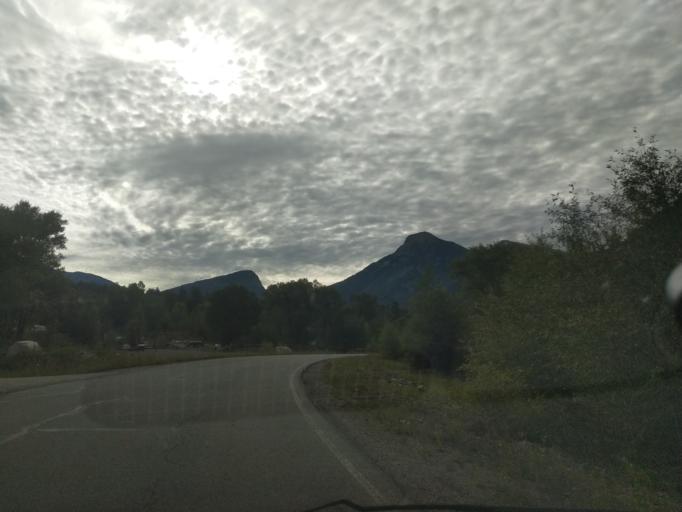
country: US
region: Colorado
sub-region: Gunnison County
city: Crested Butte
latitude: 39.0738
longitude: -107.2055
